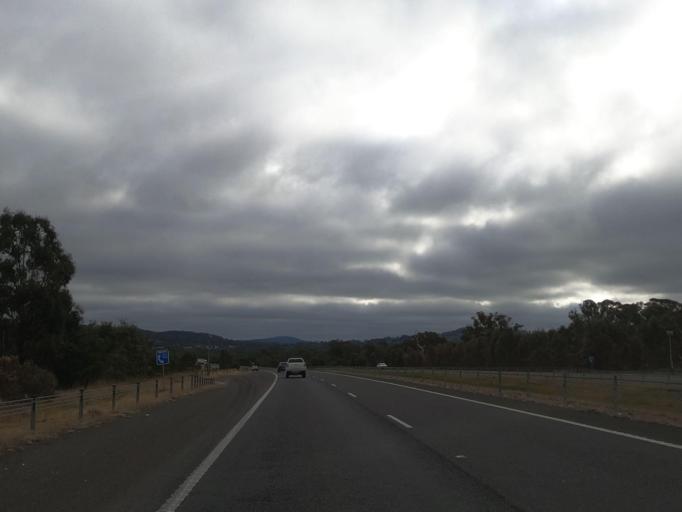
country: AU
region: Victoria
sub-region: Mount Alexander
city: Castlemaine
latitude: -37.0549
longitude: 144.2994
